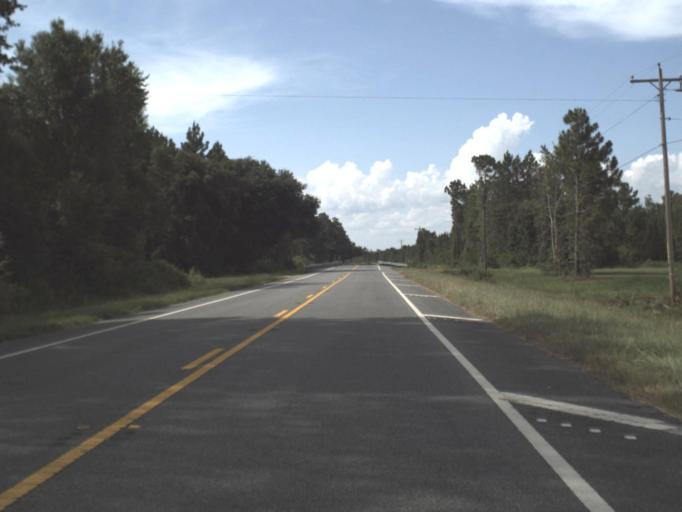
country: US
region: Florida
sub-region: Taylor County
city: Perry
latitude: 30.1979
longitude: -83.6056
